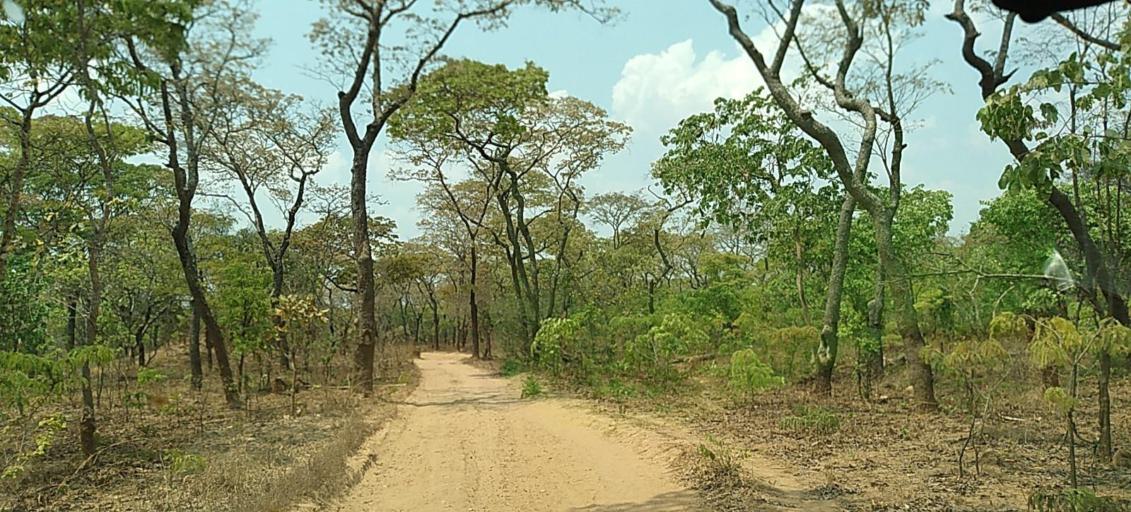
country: ZM
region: North-Western
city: Kabompo
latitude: -13.6404
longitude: 24.3824
